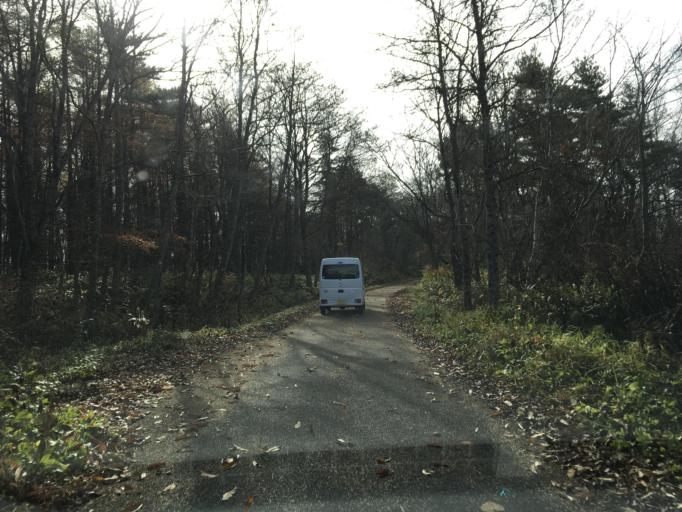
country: JP
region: Iwate
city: Mizusawa
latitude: 39.1271
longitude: 141.3031
